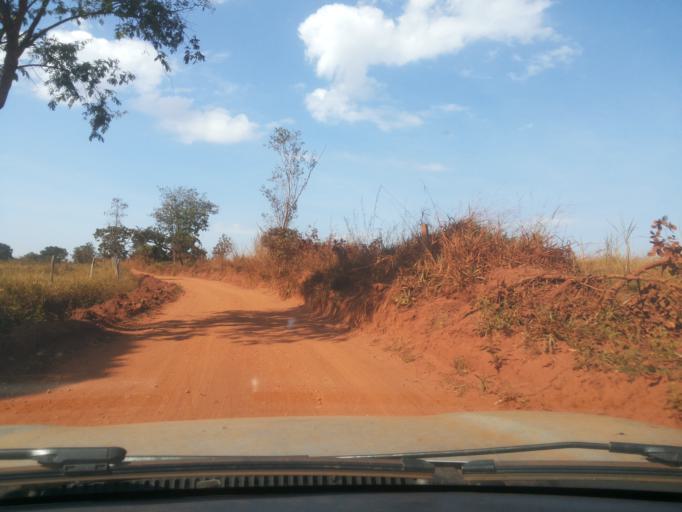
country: BR
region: Minas Gerais
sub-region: Ituiutaba
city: Ituiutaba
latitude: -19.0028
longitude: -49.4104
